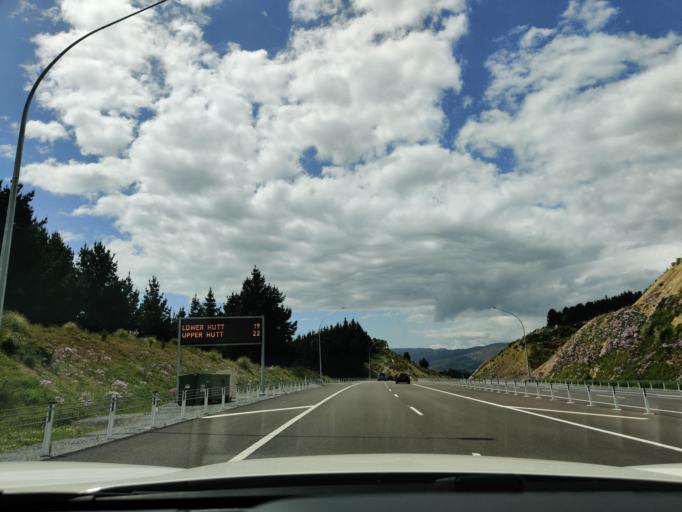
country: NZ
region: Wellington
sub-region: Porirua City
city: Porirua
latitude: -41.1249
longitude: 174.9062
